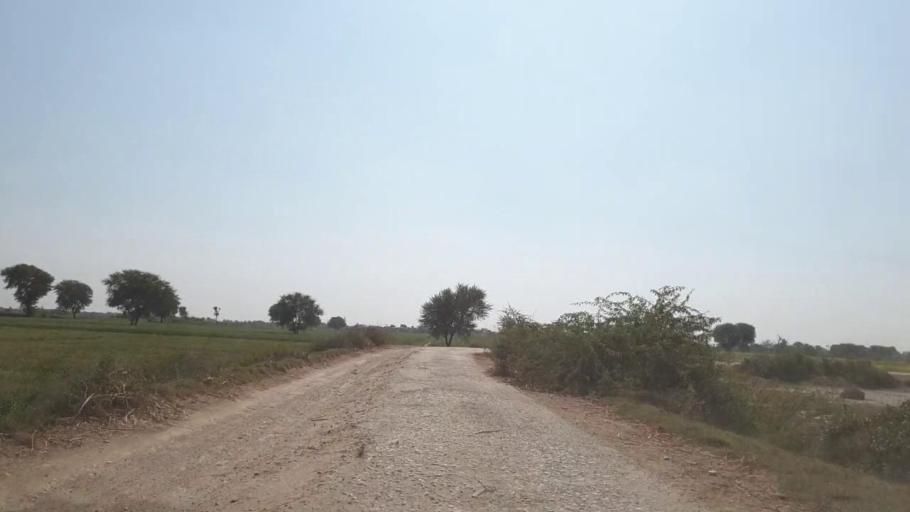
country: PK
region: Sindh
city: Mirpur Khas
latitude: 25.7371
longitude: 69.0823
